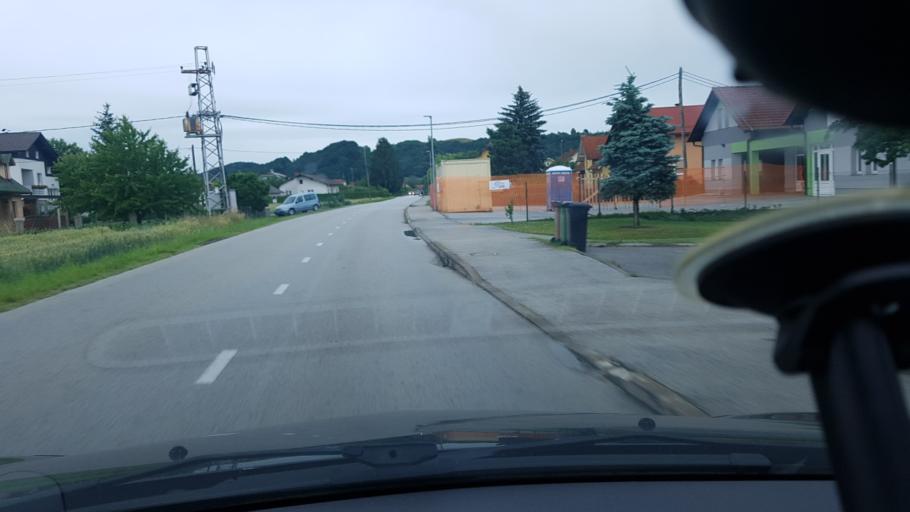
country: SI
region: Videm
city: Videm pri Ptuju
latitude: 46.3724
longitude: 15.8933
